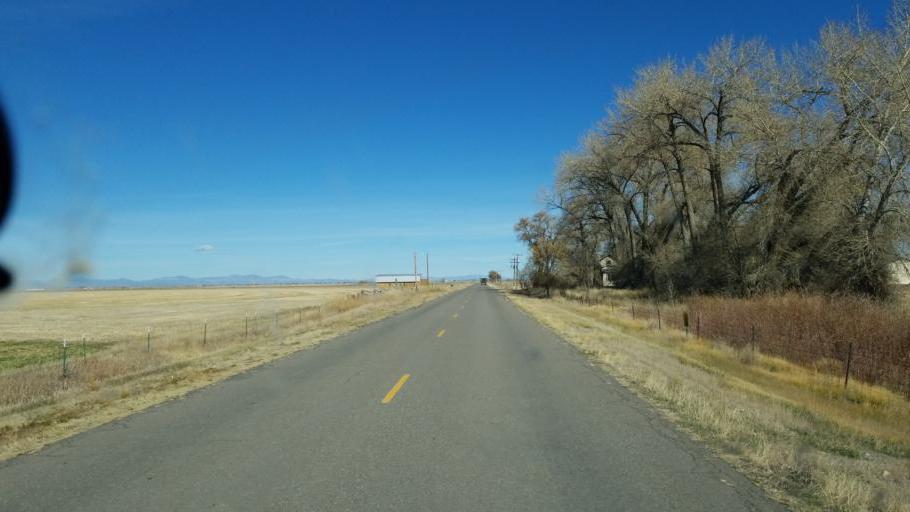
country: US
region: Colorado
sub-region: Rio Grande County
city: Monte Vista
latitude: 37.4540
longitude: -106.0942
